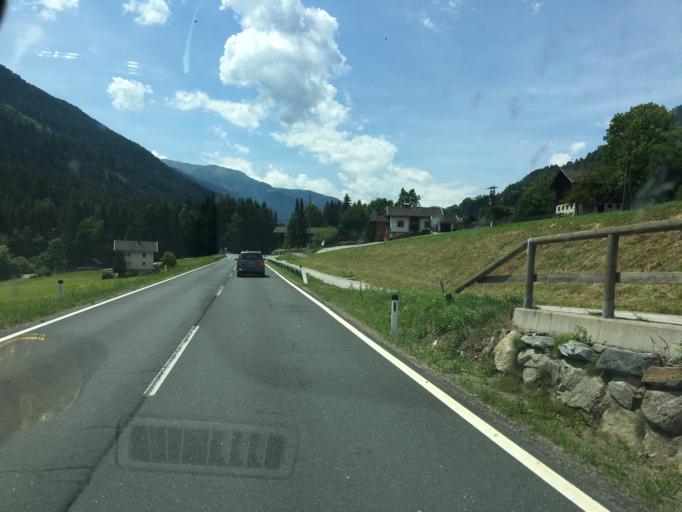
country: AT
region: Carinthia
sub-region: Politischer Bezirk Spittal an der Drau
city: Stall
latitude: 46.8812
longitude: 13.0145
